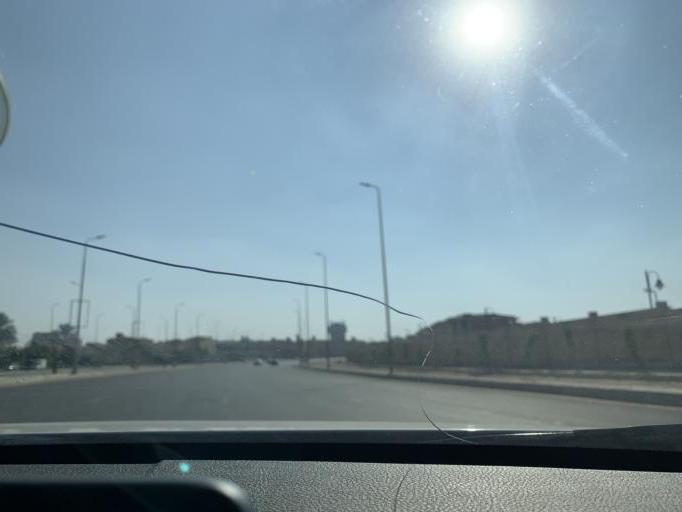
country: EG
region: Muhafazat al Qalyubiyah
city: Al Khankah
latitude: 30.0132
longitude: 31.4746
